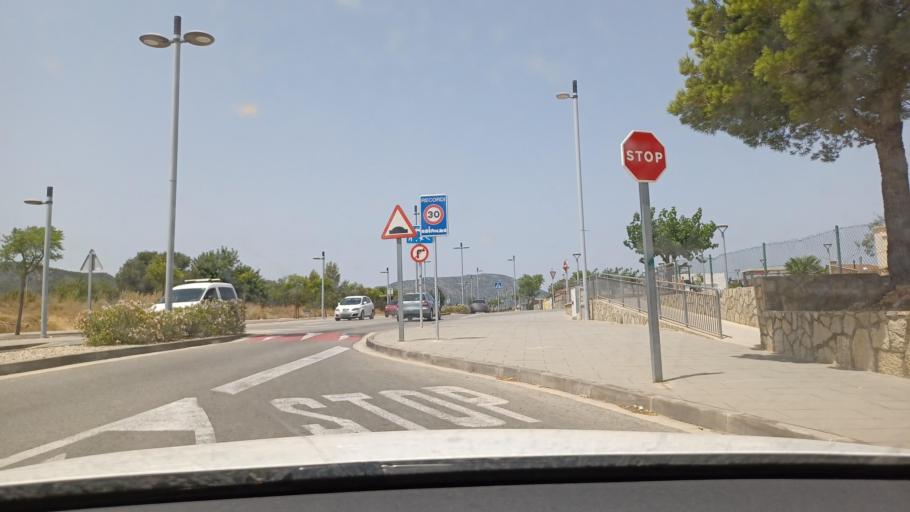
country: ES
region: Catalonia
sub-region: Provincia de Tarragona
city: Colldejou
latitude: 40.9976
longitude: 0.9186
